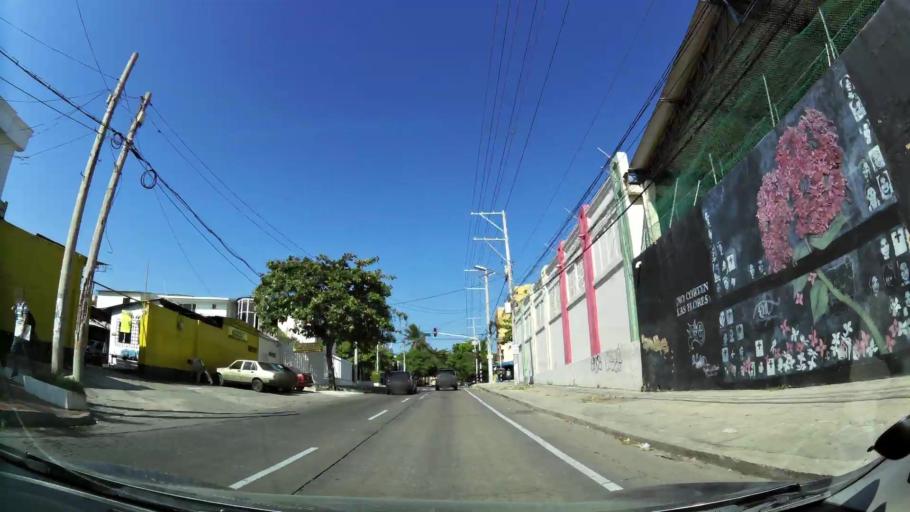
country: CO
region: Atlantico
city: Barranquilla
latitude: 10.9931
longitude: -74.8005
